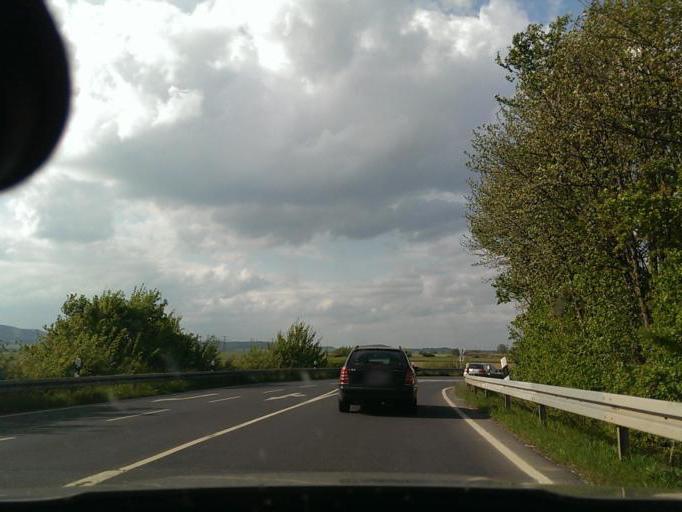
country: DE
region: Lower Saxony
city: Banteln
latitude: 52.0811
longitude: 9.7417
